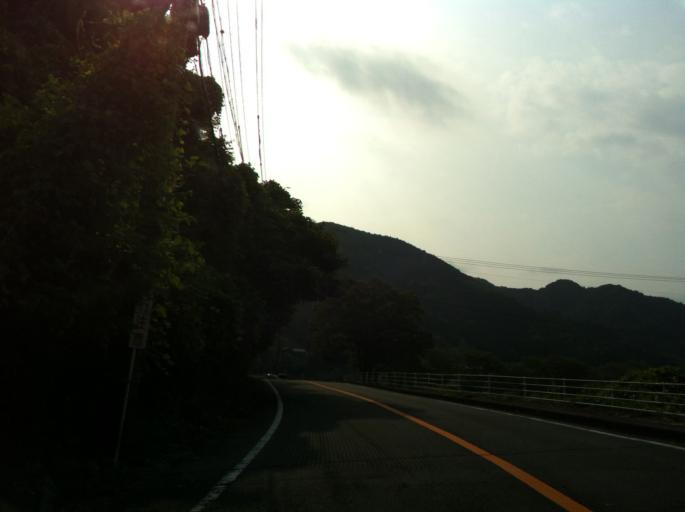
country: JP
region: Shizuoka
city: Fujieda
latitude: 34.9313
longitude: 138.2677
